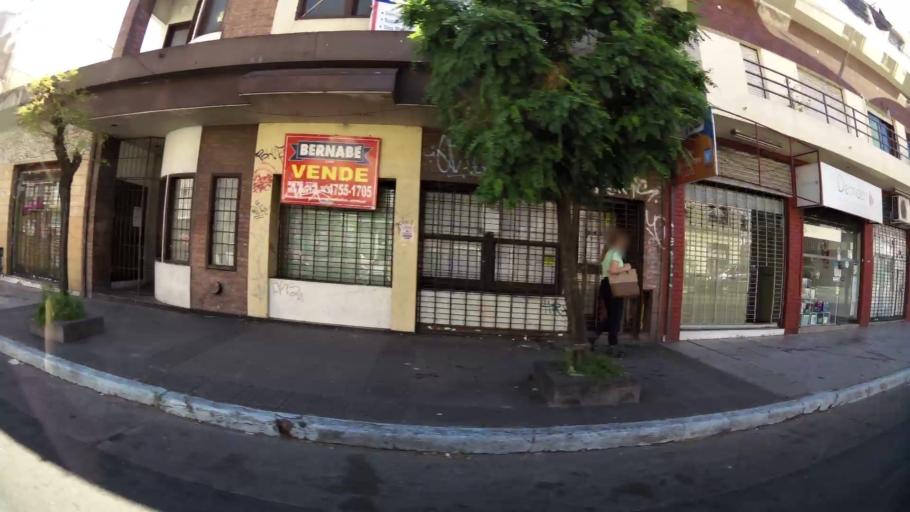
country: AR
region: Buenos Aires
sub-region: Partido de General San Martin
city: General San Martin
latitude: -34.5736
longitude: -58.5413
